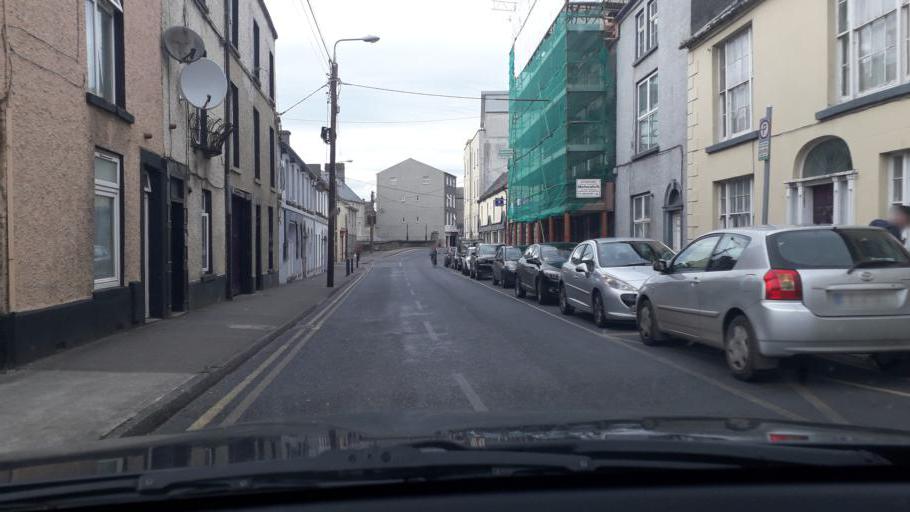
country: IE
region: Leinster
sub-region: County Carlow
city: Carlow
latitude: 52.8346
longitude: -6.9328
